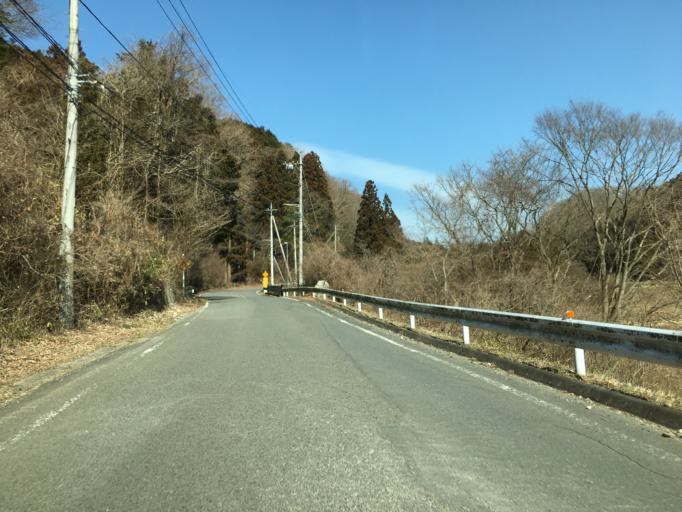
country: JP
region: Ibaraki
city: Daigo
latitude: 36.8096
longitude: 140.5011
